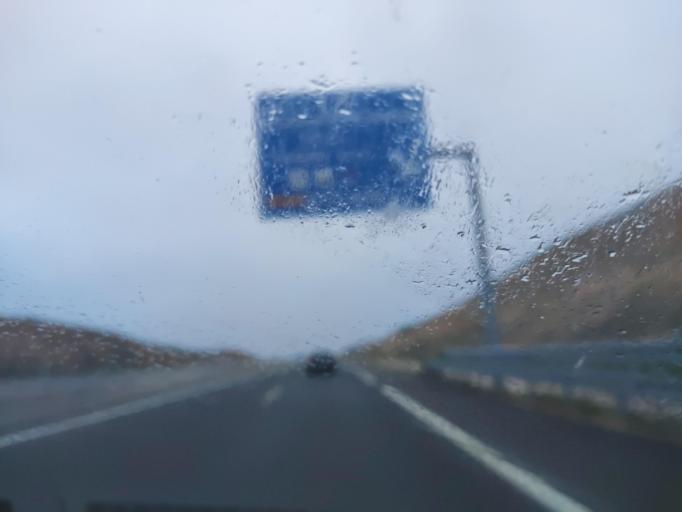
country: ES
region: Castille-La Mancha
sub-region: Province of Toledo
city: Bargas
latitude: 39.9097
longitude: -4.0587
